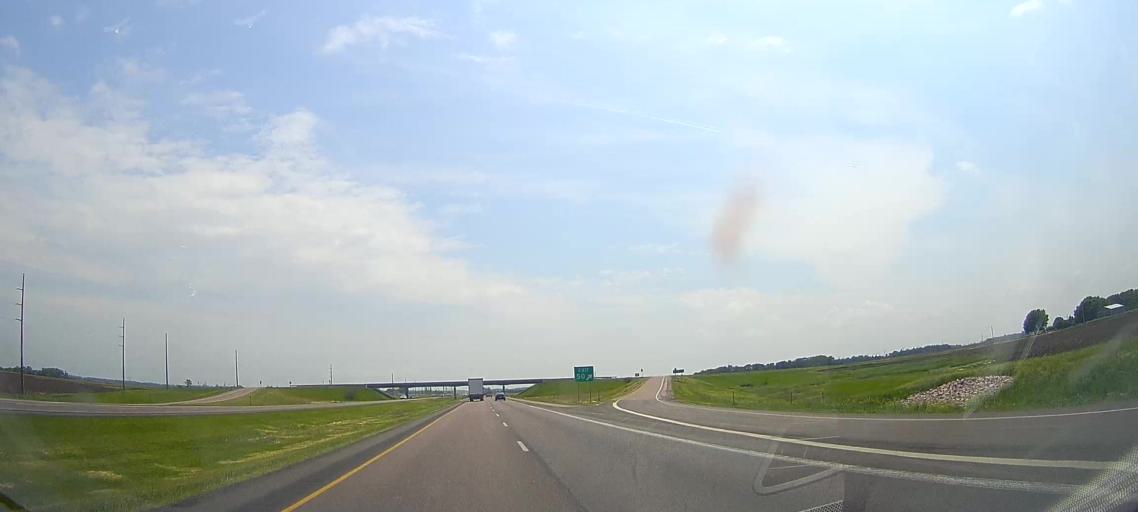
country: US
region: South Dakota
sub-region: Union County
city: Beresford
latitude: 43.1294
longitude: -96.7969
